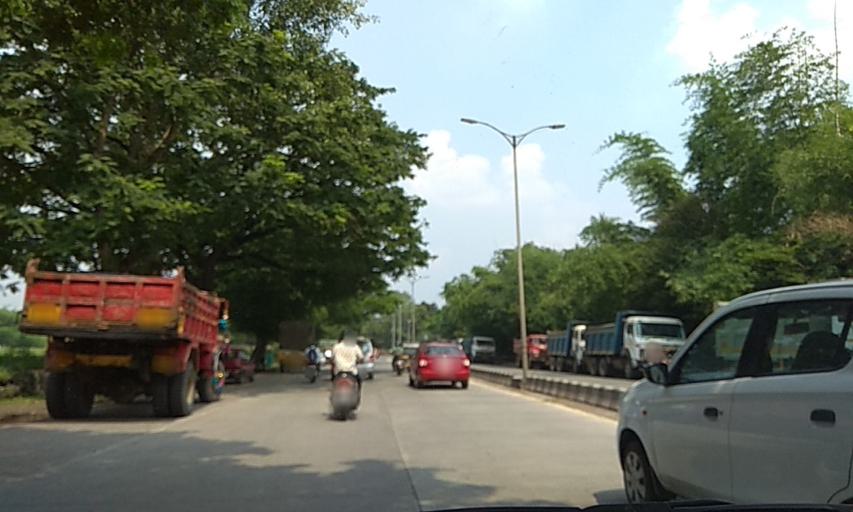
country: IN
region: Maharashtra
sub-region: Pune Division
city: Khadki
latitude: 18.5496
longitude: 73.8516
